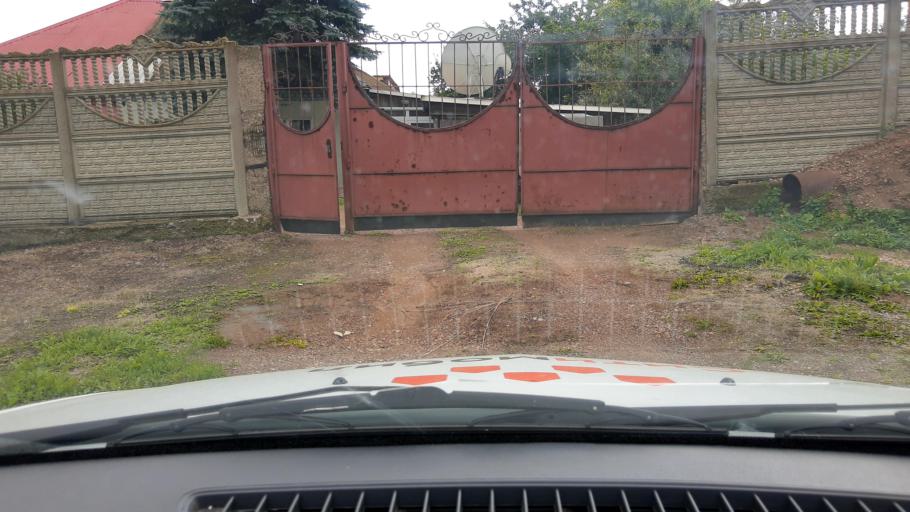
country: RU
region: Bashkortostan
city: Iglino
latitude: 54.9057
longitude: 56.1998
